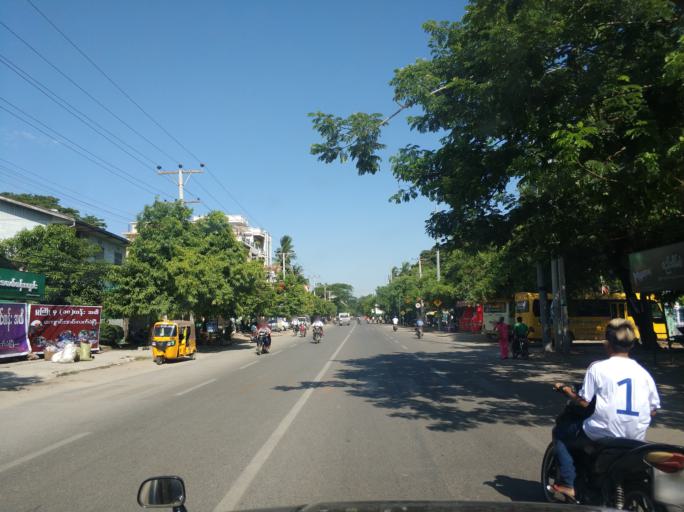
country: MM
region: Mandalay
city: Mandalay
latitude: 21.9705
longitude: 96.0666
